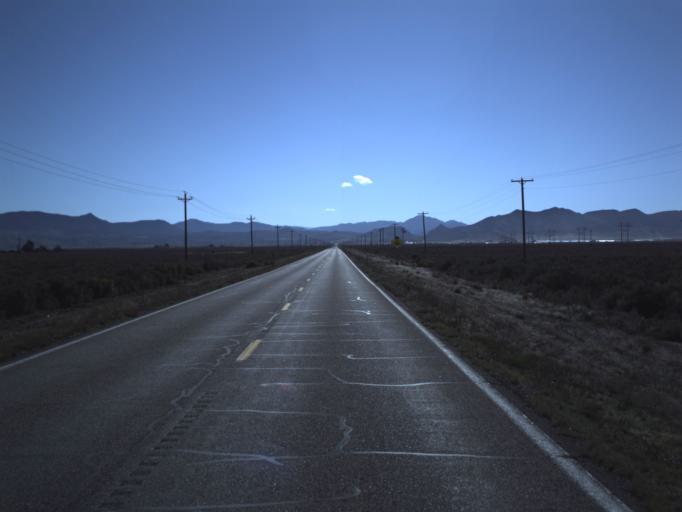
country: US
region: Utah
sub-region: Washington County
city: Enterprise
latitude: 37.7028
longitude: -113.6378
